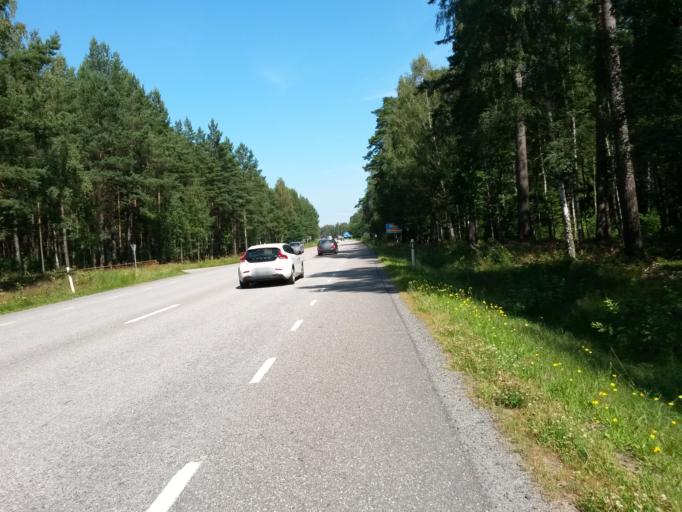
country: SE
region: Vaestra Goetaland
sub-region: Lidkopings Kommun
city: Lidkoping
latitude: 58.4885
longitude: 13.1348
